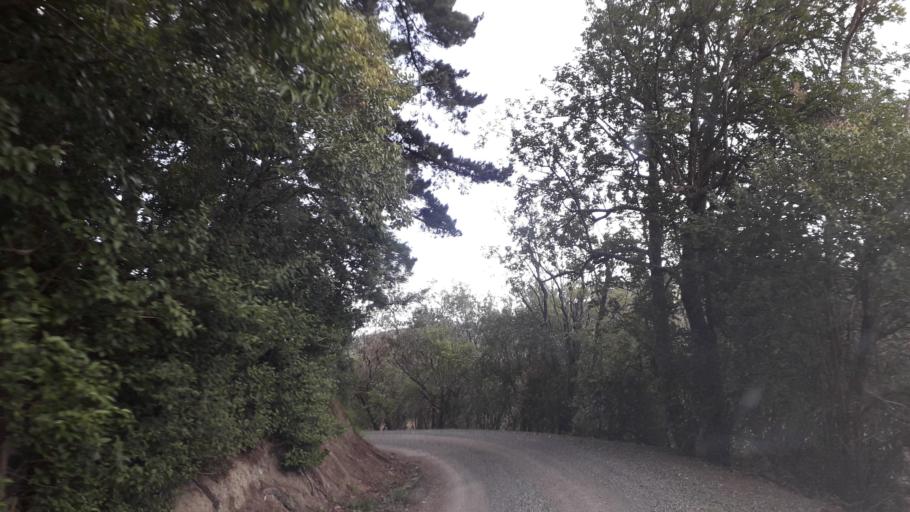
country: NZ
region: Northland
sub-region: Far North District
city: Waimate North
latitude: -35.3157
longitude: 173.5682
